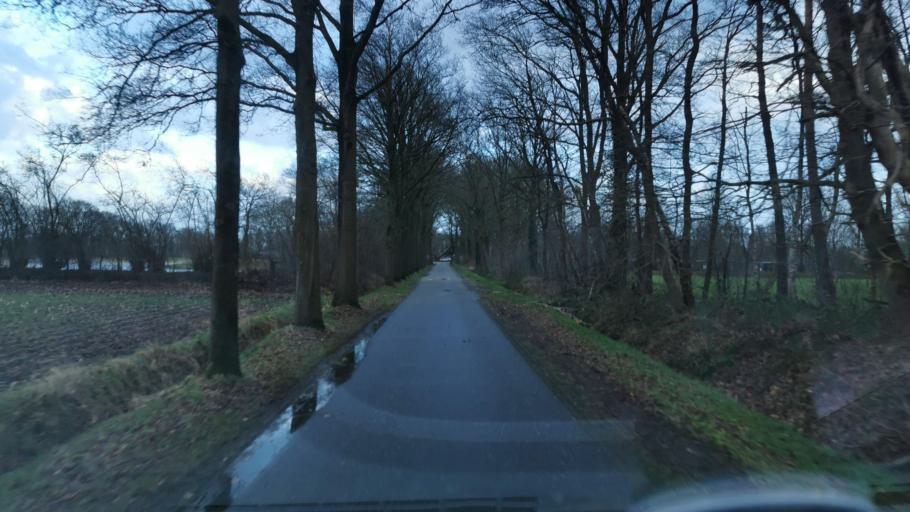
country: DE
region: Lower Saxony
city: Lage
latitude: 52.4270
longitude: 6.9889
